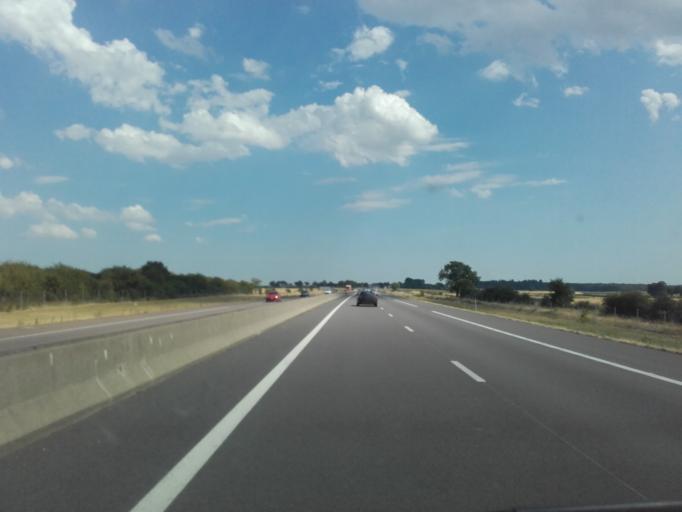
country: FR
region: Bourgogne
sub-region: Departement de la Cote-d'Or
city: Semur-en-Auxois
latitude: 47.4827
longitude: 4.1749
